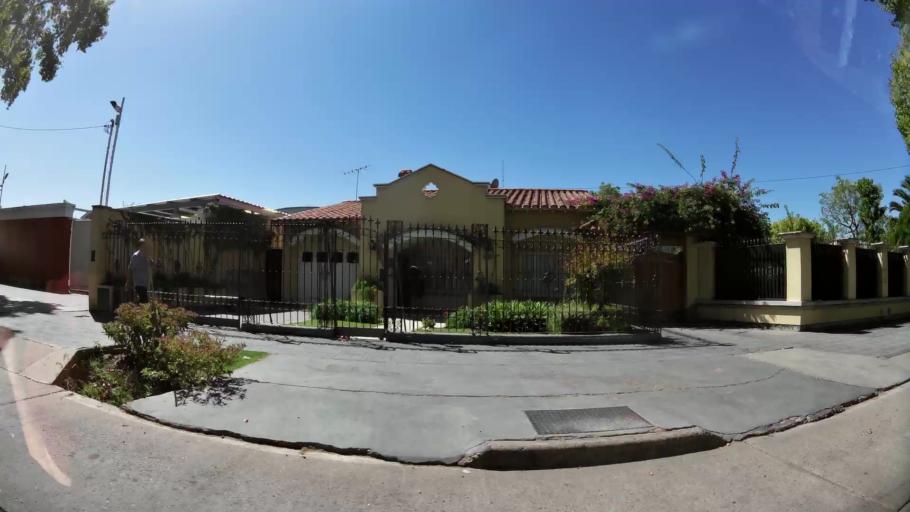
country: AR
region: Mendoza
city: Villa Nueva
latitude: -32.8978
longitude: -68.7976
